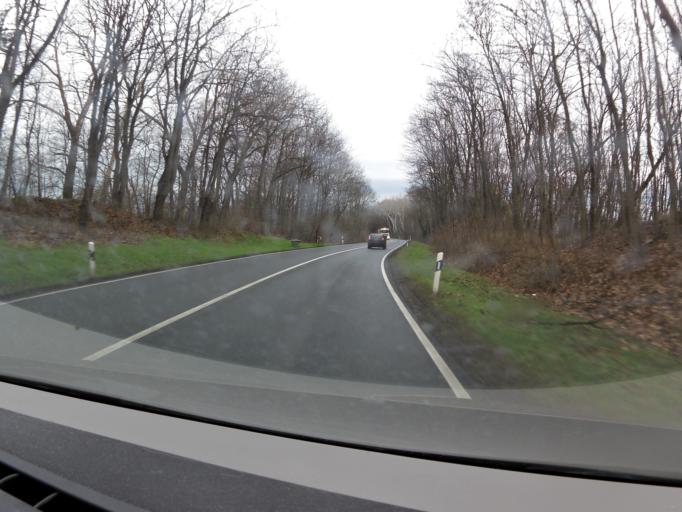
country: DE
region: Saxony-Anhalt
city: Aschersleben
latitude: 51.7393
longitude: 11.4548
